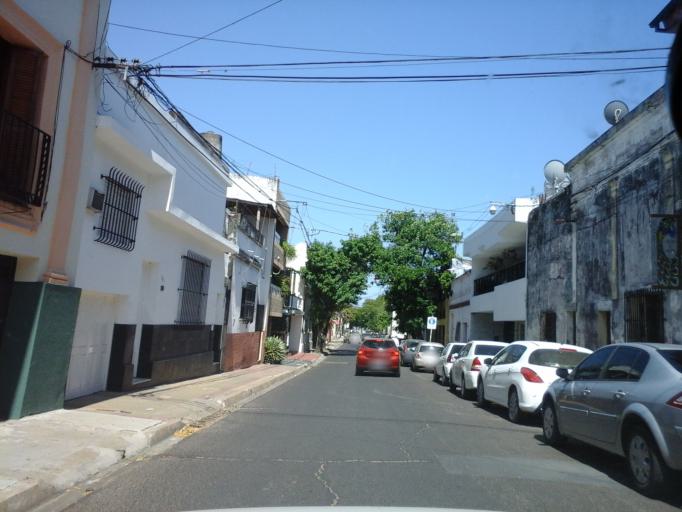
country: AR
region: Corrientes
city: Corrientes
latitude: -27.4627
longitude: -58.8404
